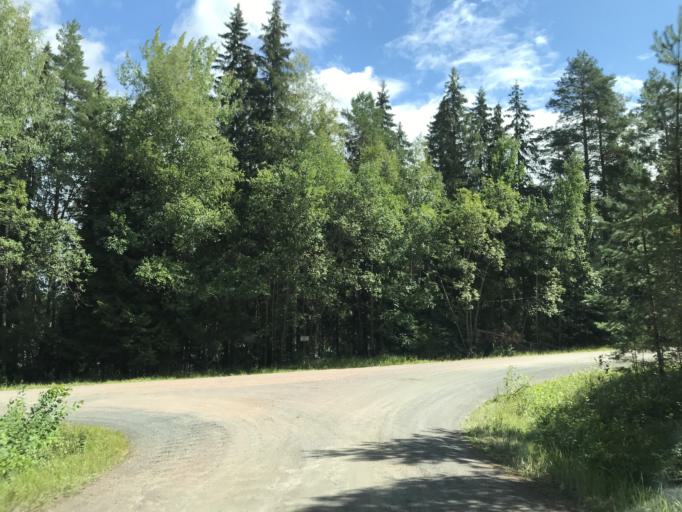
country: FI
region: Uusimaa
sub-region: Helsinki
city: Kaerkoelae
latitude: 60.6254
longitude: 23.7716
